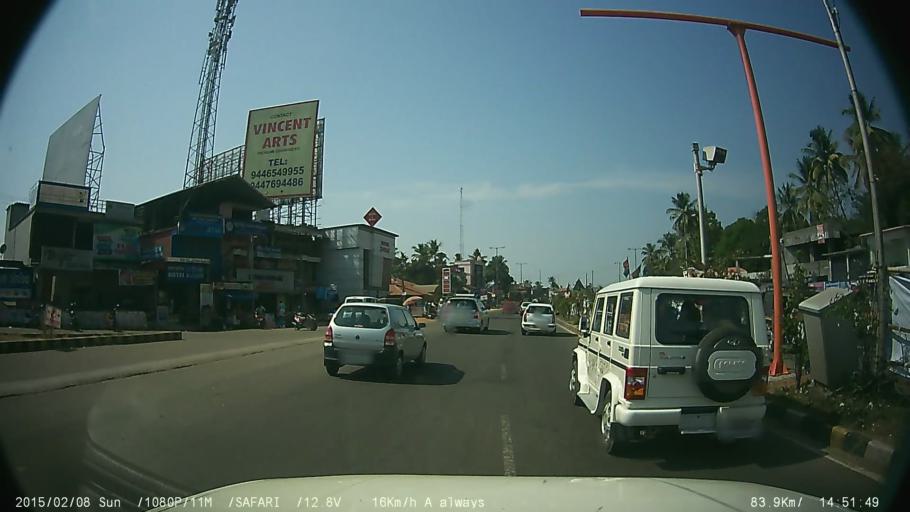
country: IN
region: Kerala
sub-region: Thrissur District
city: Kizhake Chalakudi
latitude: 10.2681
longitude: 76.3495
